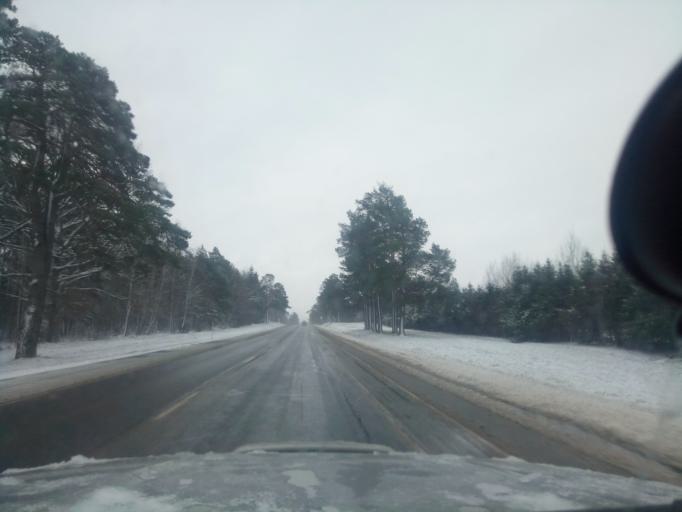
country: BY
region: Minsk
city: Nyasvizh
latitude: 53.2543
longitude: 26.6172
